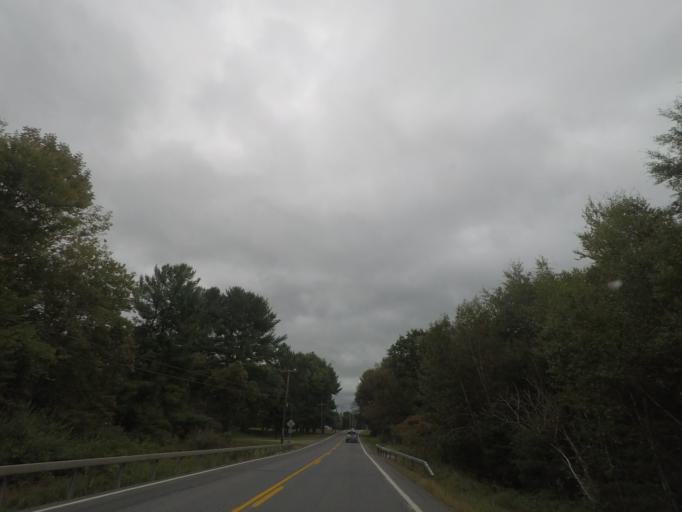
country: US
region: New York
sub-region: Washington County
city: Cambridge
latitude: 42.9527
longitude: -73.4259
